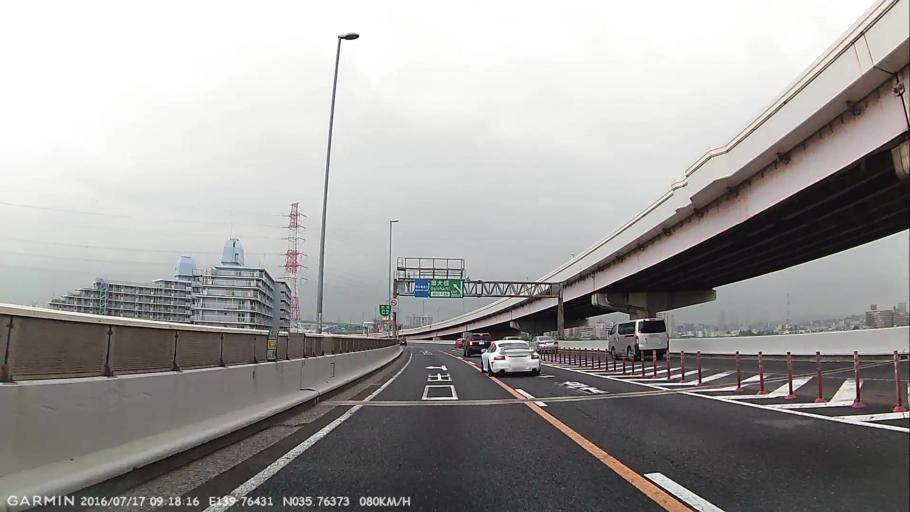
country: JP
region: Saitama
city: Kawaguchi
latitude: 35.7637
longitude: 139.7643
